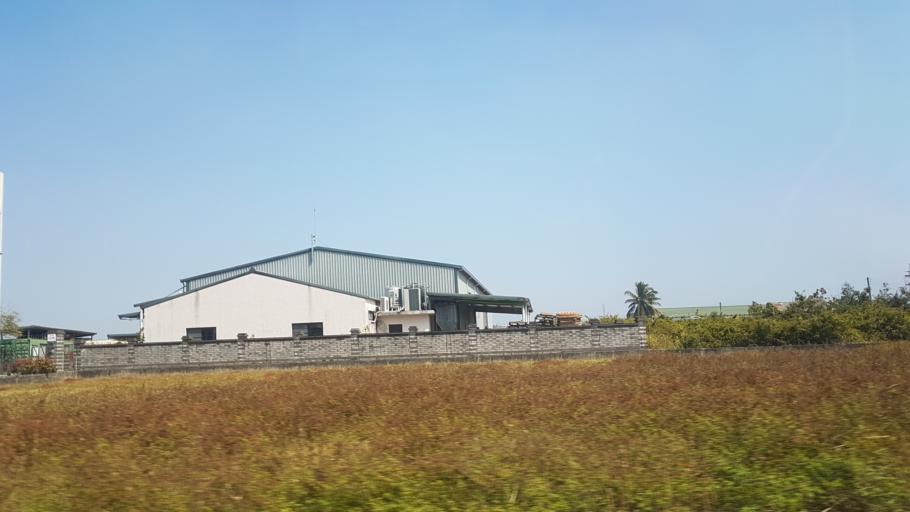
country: TW
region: Taiwan
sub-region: Tainan
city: Tainan
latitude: 22.9336
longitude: 120.2510
